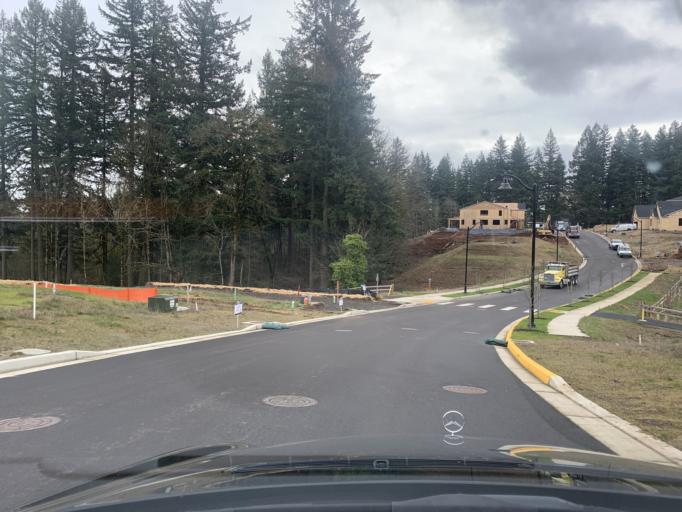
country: US
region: Oregon
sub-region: Clackamas County
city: Happy Valley
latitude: 45.4417
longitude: -122.5084
